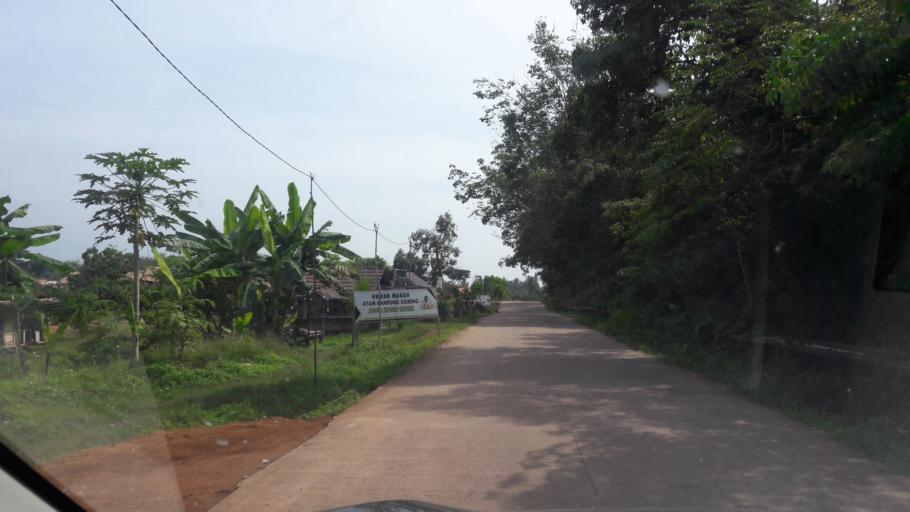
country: ID
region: South Sumatra
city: Gunungmenang
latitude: -3.3167
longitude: 104.1140
